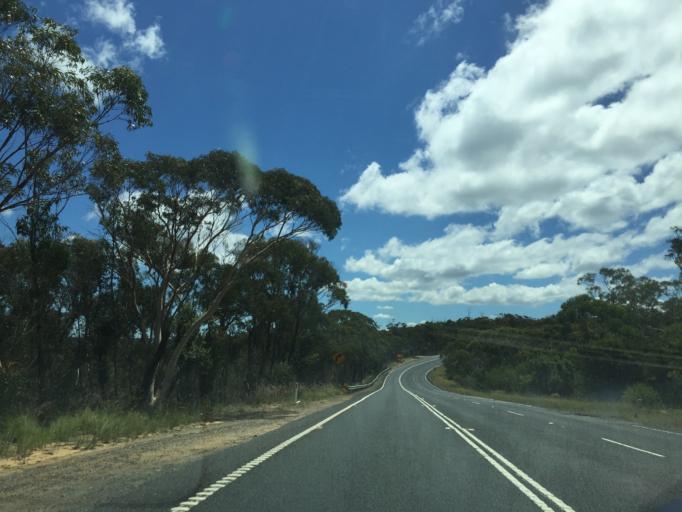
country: AU
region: New South Wales
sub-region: Blue Mountains Municipality
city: Blackheath
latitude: -33.5673
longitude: 150.3476
